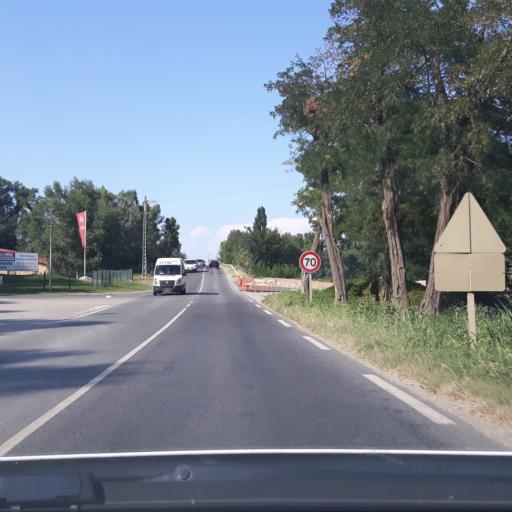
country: FR
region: Midi-Pyrenees
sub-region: Departement de la Haute-Garonne
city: Ondes
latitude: 43.7753
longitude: 1.3056
